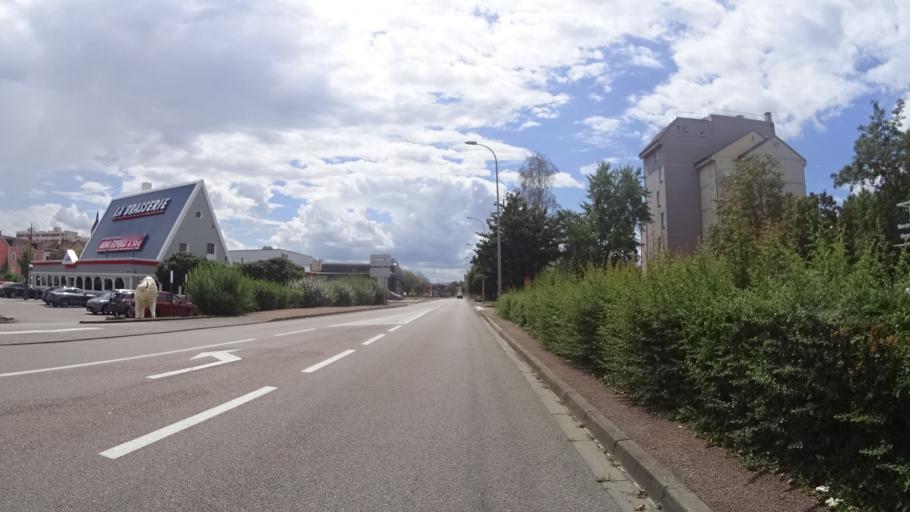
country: FR
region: Bourgogne
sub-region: Departement de Saone-et-Loire
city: Montceau-les-Mines
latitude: 46.6782
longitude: 4.3644
